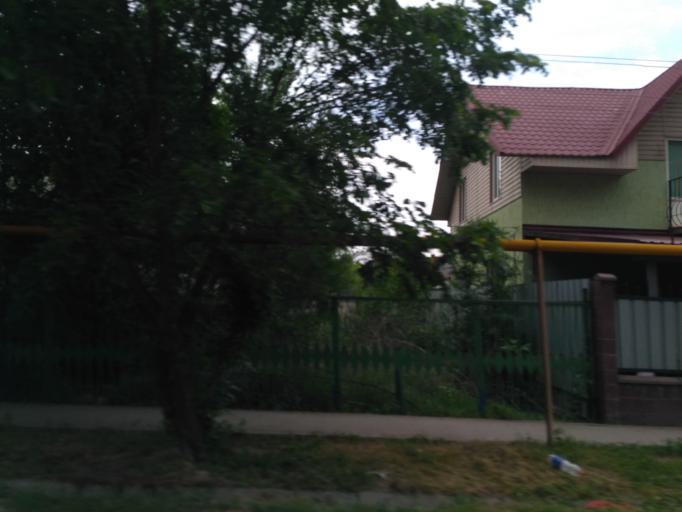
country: KZ
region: Almaty Oblysy
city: Burunday
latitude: 43.4597
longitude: 76.7258
